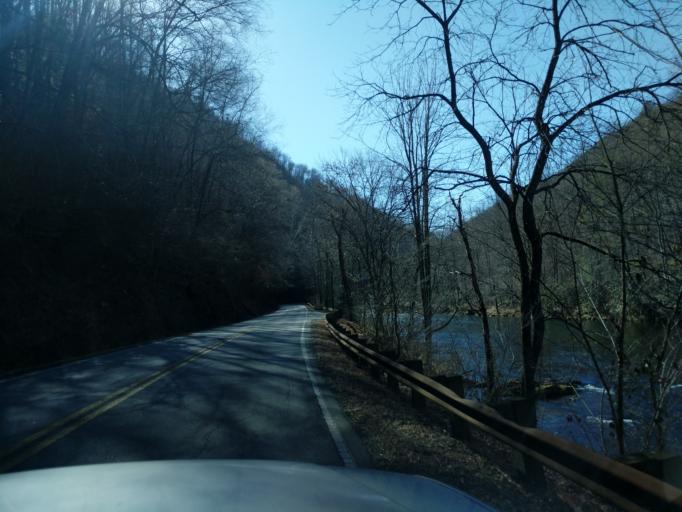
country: US
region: North Carolina
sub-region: Graham County
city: Robbinsville
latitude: 35.3249
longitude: -83.6304
